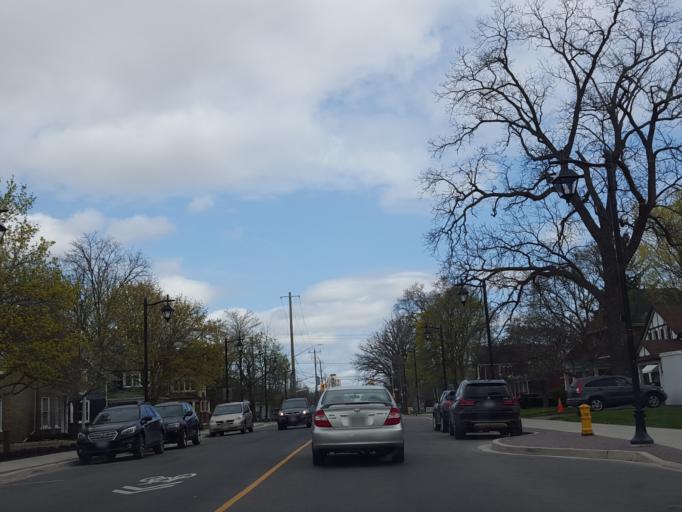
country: CA
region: Ontario
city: Markham
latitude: 43.8799
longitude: -79.2612
